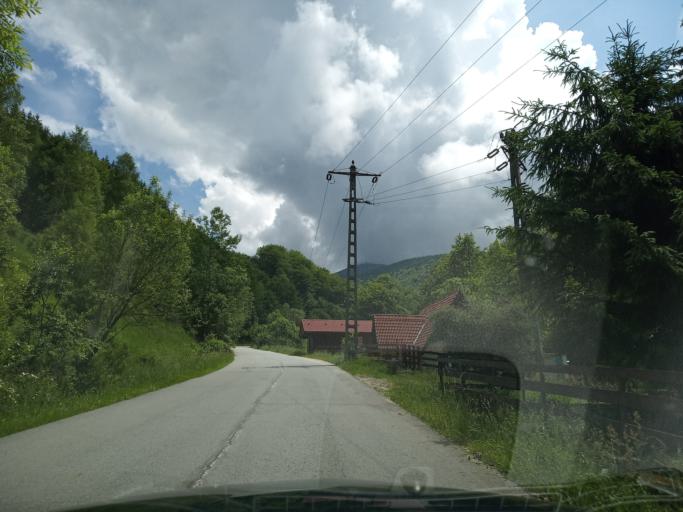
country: RO
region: Hunedoara
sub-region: Oras Petrila
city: Petrila
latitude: 45.3959
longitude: 23.4351
